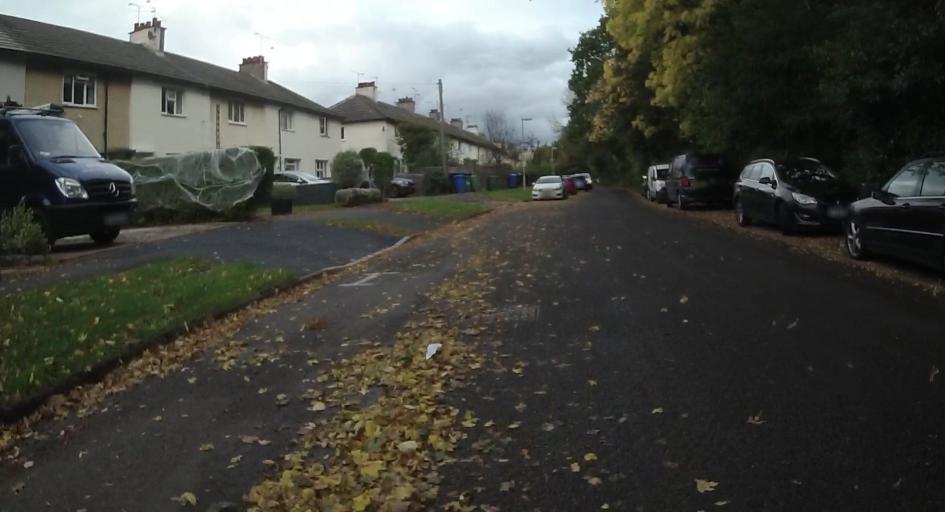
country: GB
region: England
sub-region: Hampshire
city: Farnborough
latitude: 51.2865
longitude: -0.7702
